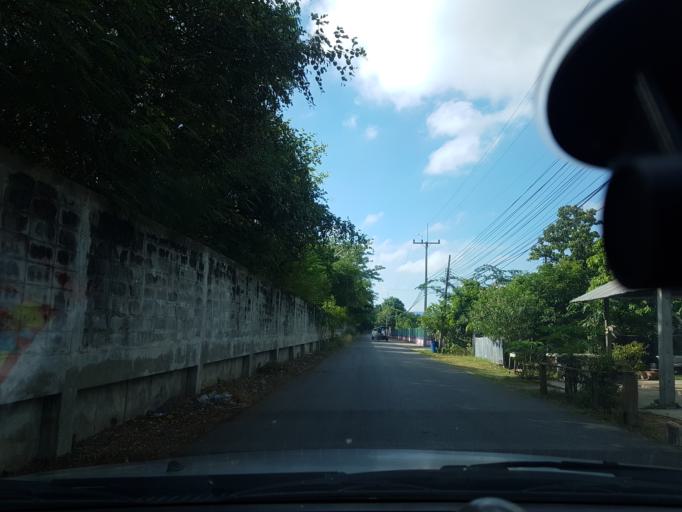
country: TH
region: Lop Buri
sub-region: Amphoe Tha Luang
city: Tha Luang
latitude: 15.0768
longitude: 101.0521
